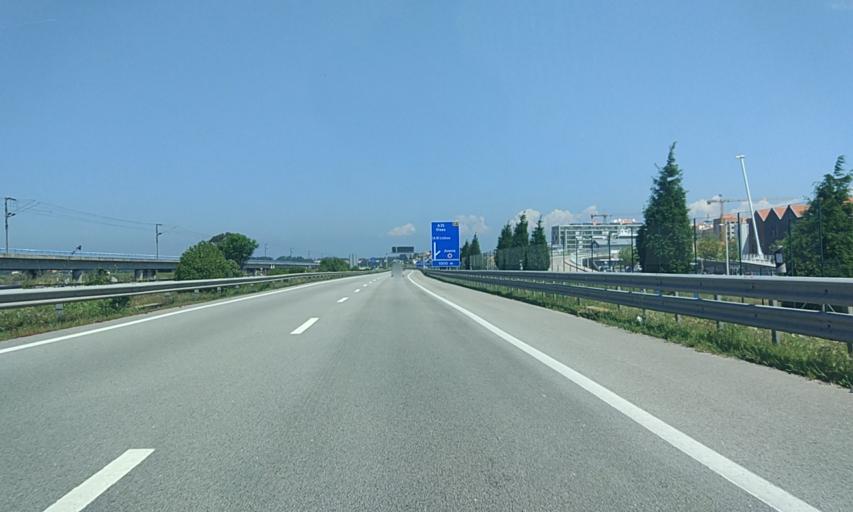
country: PT
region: Aveiro
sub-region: Aveiro
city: Aveiro
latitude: 40.6459
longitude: -8.6542
